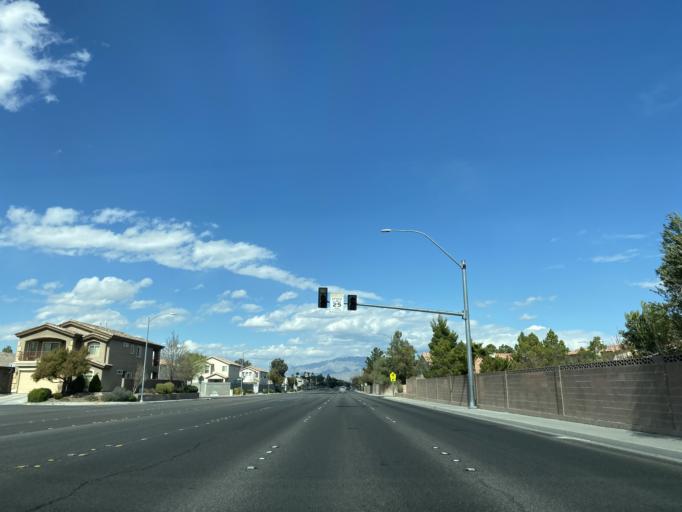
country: US
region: Nevada
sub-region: Clark County
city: Spring Valley
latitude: 36.2284
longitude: -115.2606
